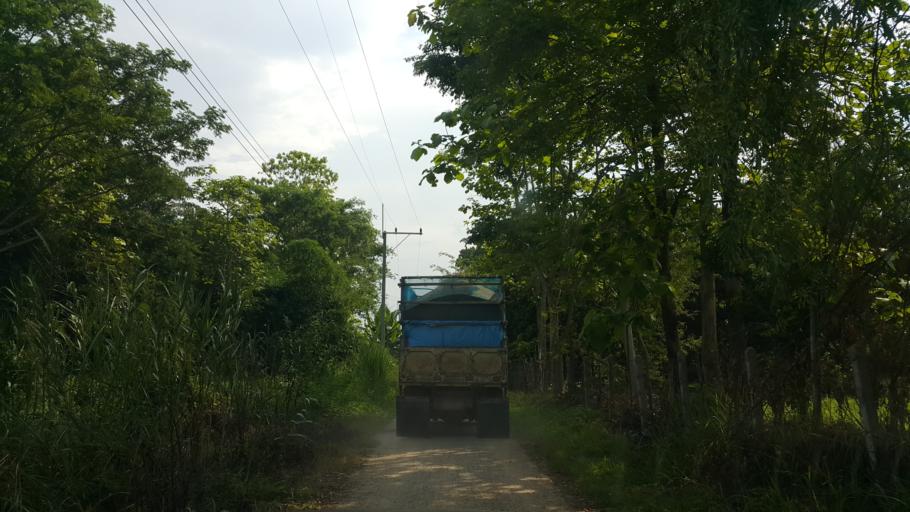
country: TH
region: Chiang Rai
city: Wiang Chai
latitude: 19.9137
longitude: 99.9055
